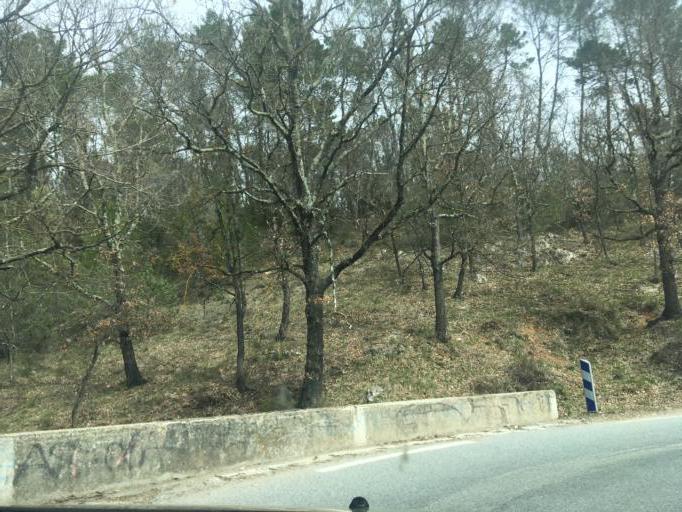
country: FR
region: Provence-Alpes-Cote d'Azur
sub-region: Departement du Var
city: Saint-Paul-en-Foret
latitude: 43.5875
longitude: 6.7292
